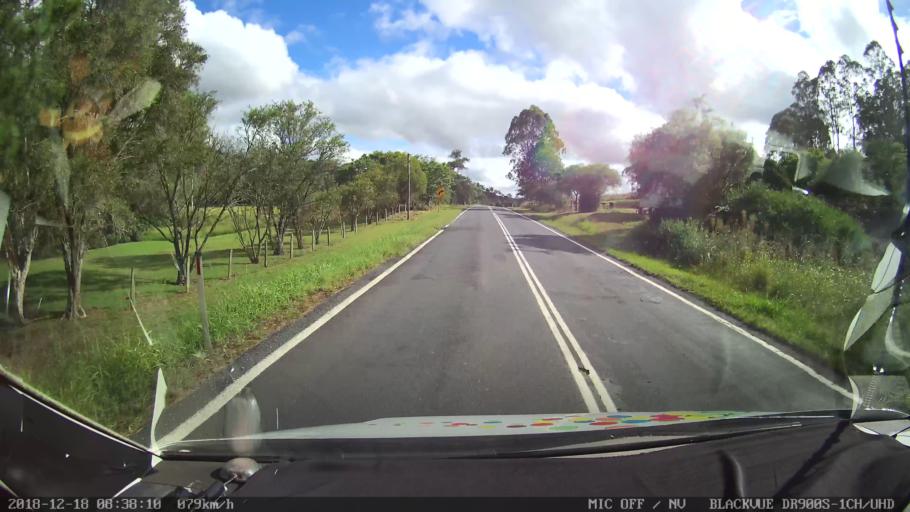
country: AU
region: New South Wales
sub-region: Kyogle
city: Kyogle
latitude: -28.2582
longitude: 152.8250
